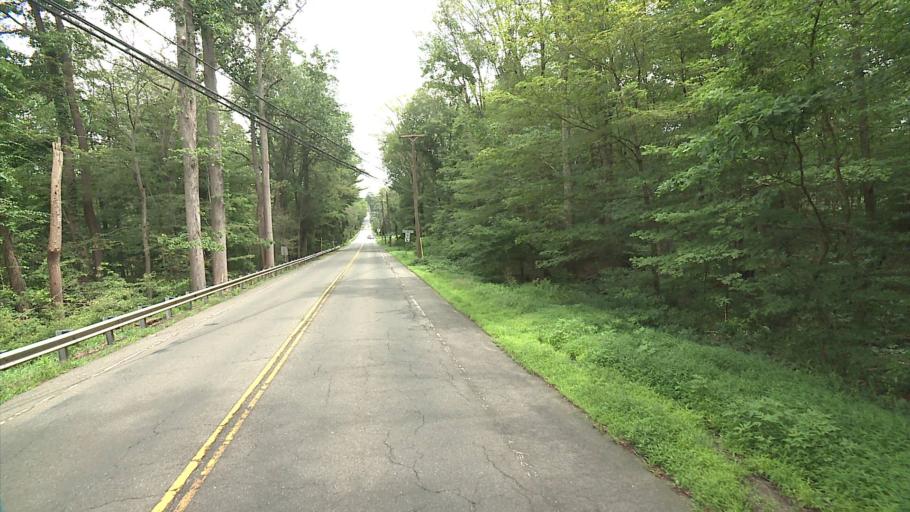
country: US
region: Connecticut
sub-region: Middlesex County
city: Chester Center
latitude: 41.3591
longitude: -72.5023
